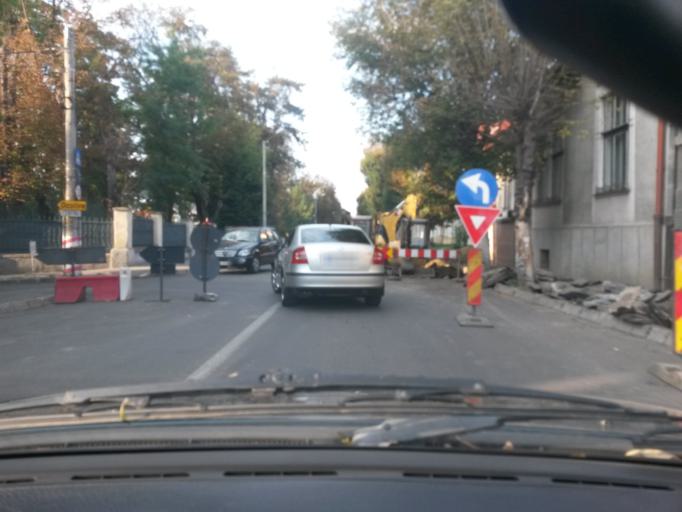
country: RO
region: Mures
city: Targu-Mures
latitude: 46.5481
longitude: 24.5723
